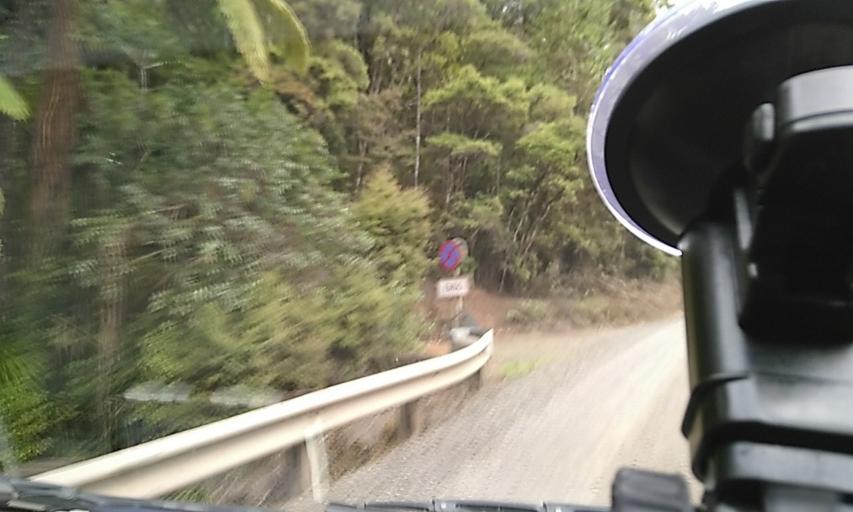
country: NZ
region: Northland
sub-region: Kaipara District
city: Dargaville
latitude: -35.6530
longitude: 173.5602
